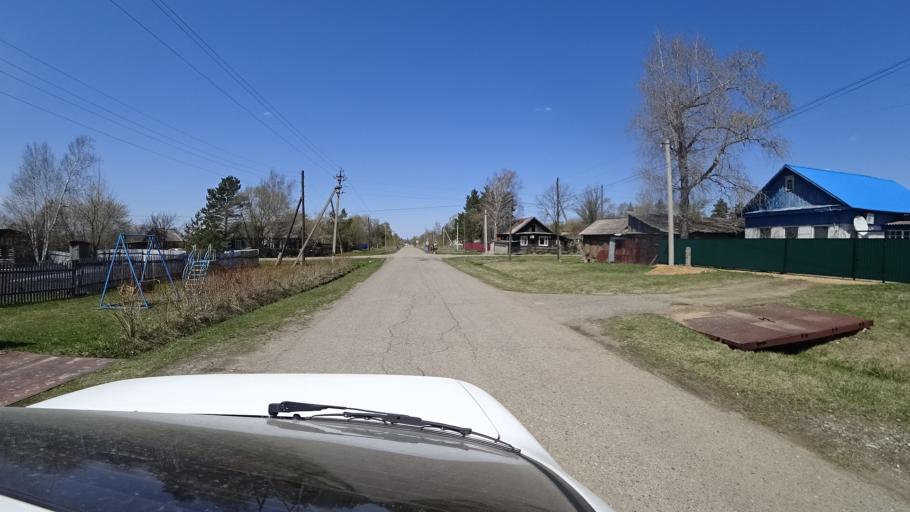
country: RU
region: Primorskiy
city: Lazo
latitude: 45.7936
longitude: 133.7664
